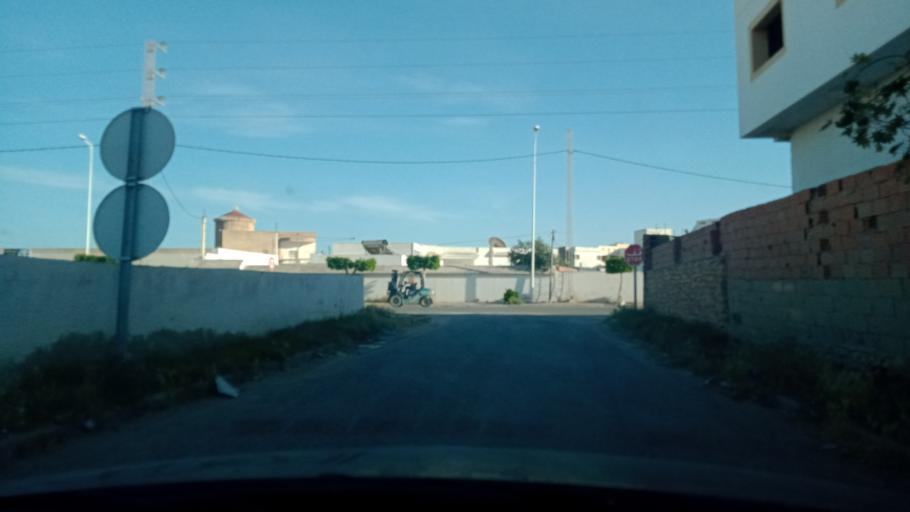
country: TN
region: Safaqis
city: Sfax
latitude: 34.8150
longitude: 10.7362
